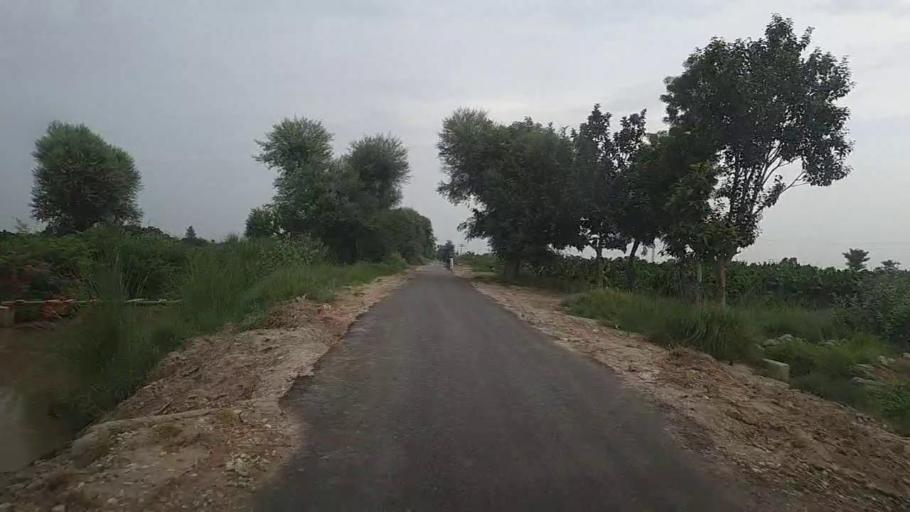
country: PK
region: Sindh
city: Karaundi
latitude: 26.9819
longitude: 68.3564
